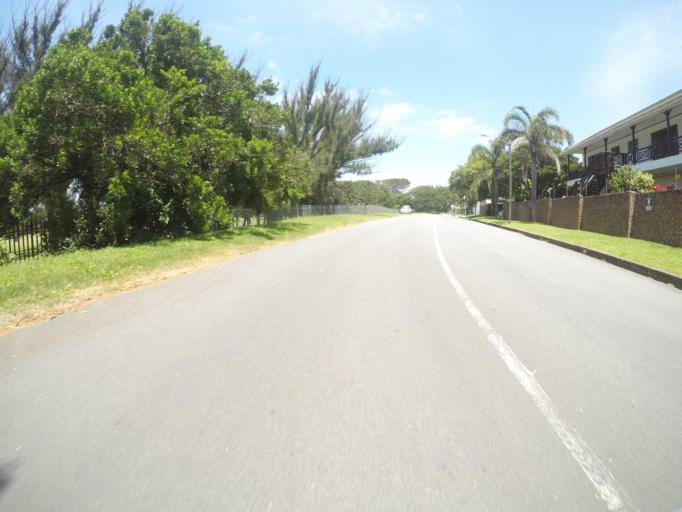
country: ZA
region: Eastern Cape
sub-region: Buffalo City Metropolitan Municipality
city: East London
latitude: -32.9964
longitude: 27.9320
